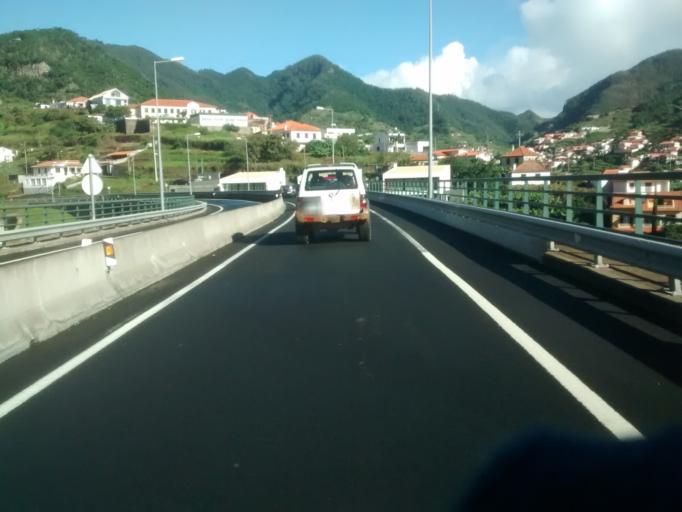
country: PT
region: Madeira
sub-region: Machico
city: Machico
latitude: 32.7283
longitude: -16.7790
